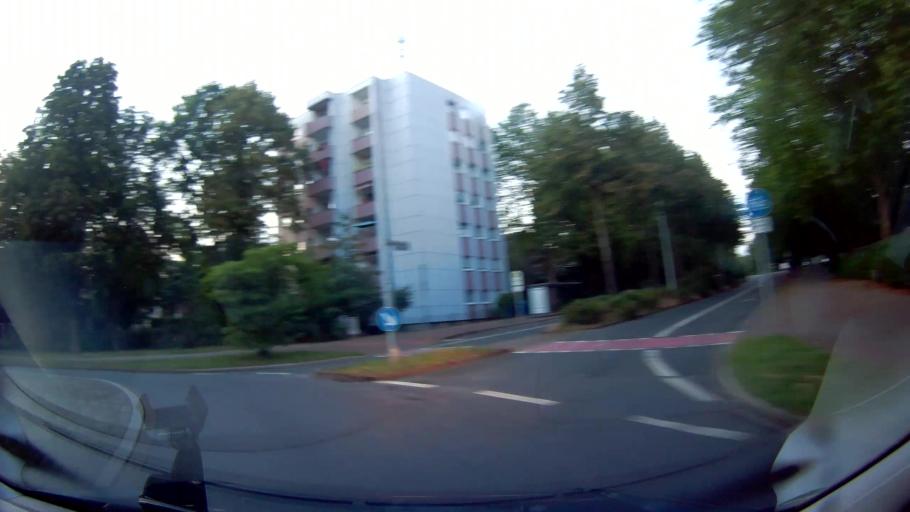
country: DE
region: North Rhine-Westphalia
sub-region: Regierungsbezirk Munster
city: Gladbeck
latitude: 51.5287
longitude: 7.0275
